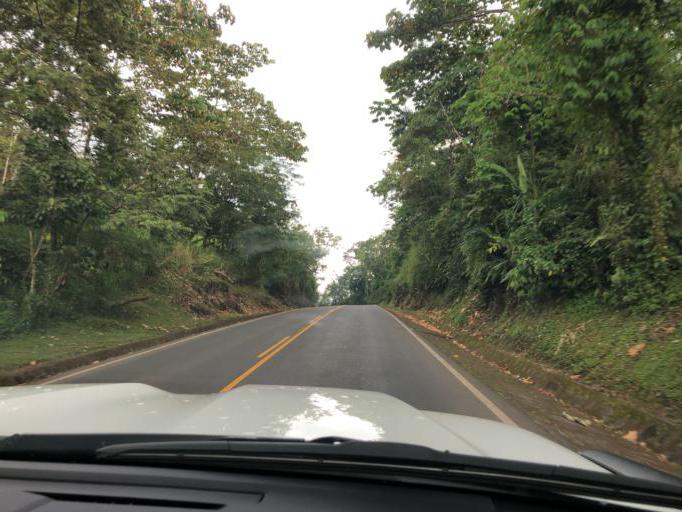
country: NI
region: Chontales
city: Villa Sandino
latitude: 11.9899
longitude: -84.8118
